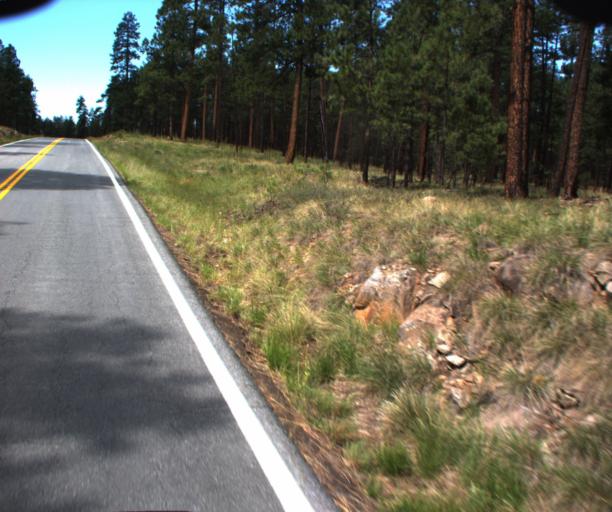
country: US
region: Arizona
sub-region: Apache County
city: Eagar
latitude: 33.7643
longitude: -109.2064
